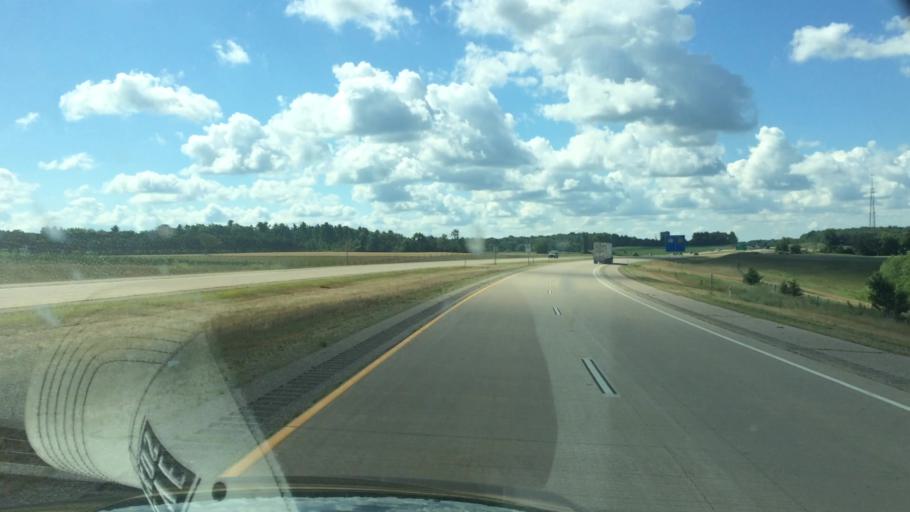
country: US
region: Wisconsin
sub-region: Portage County
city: Amherst
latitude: 44.4619
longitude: -89.3135
